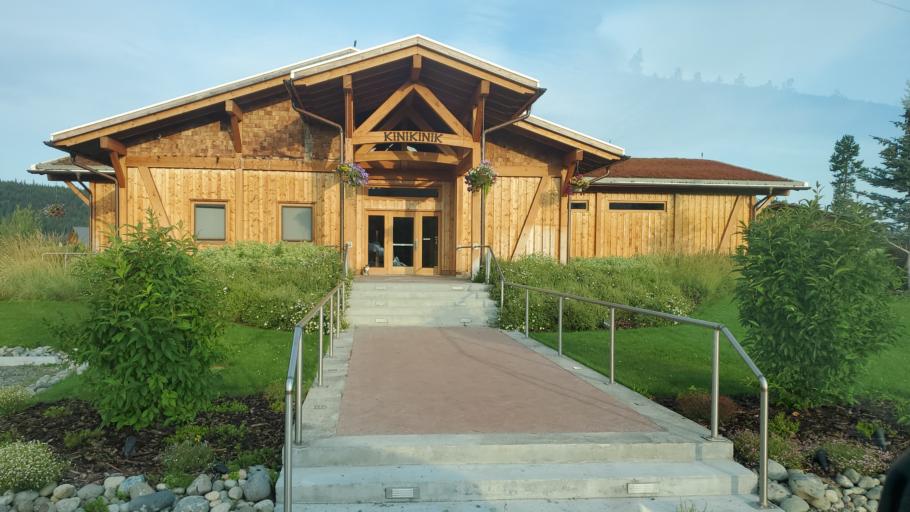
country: CA
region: British Columbia
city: Hanceville
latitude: 52.1319
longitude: -123.6983
